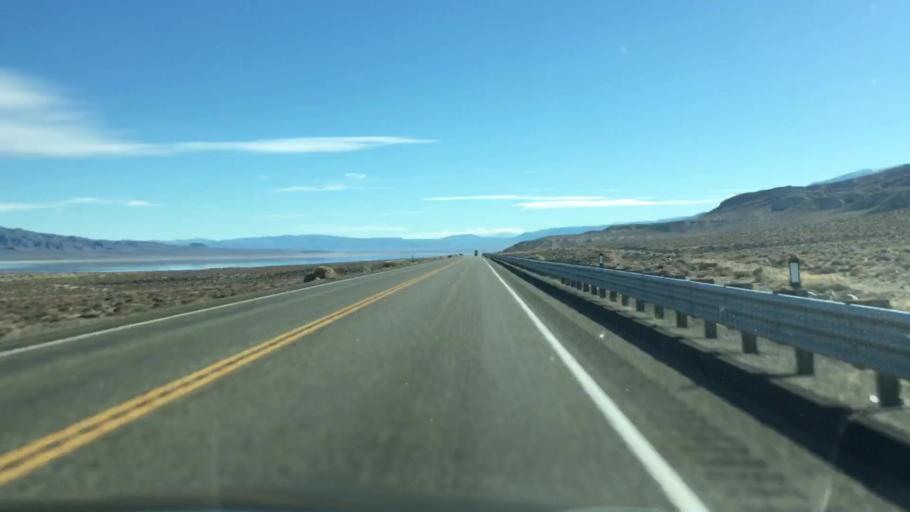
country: US
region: Nevada
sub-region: Mineral County
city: Hawthorne
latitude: 38.7962
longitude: -118.7583
